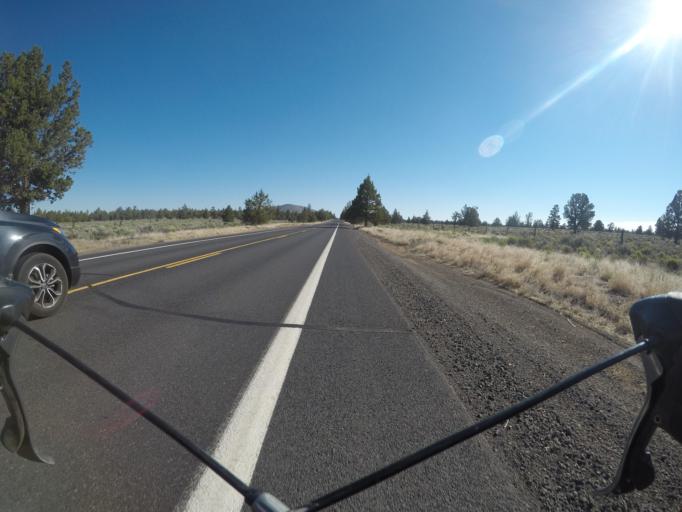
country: US
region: Oregon
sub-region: Deschutes County
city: Bend
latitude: 44.2117
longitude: -121.3173
